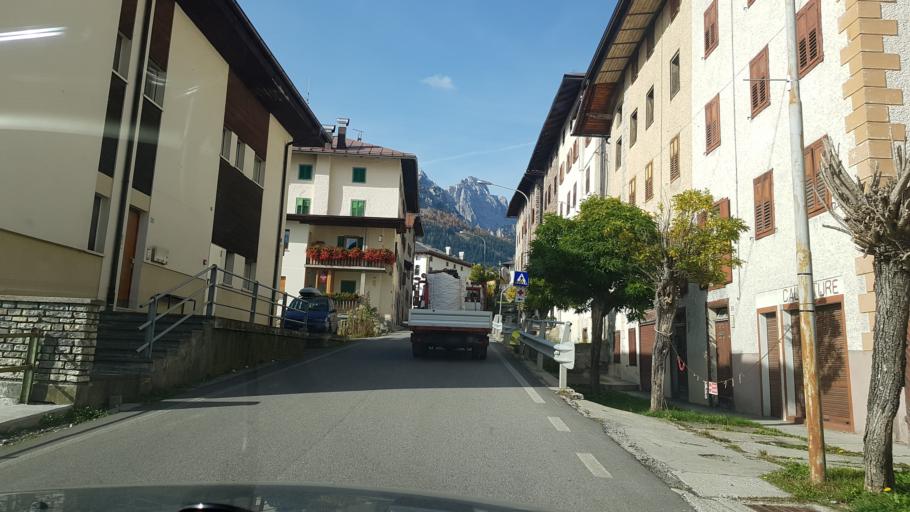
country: IT
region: Veneto
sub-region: Provincia di Belluno
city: Candide
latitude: 46.5993
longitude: 12.4936
